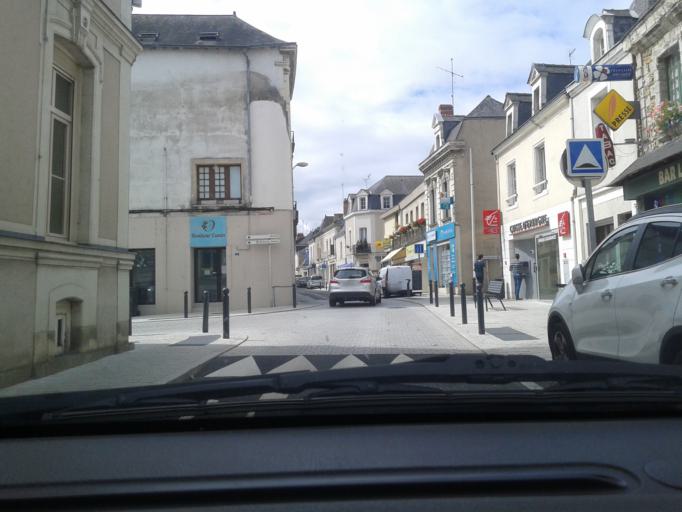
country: FR
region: Pays de la Loire
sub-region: Departement de Maine-et-Loire
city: Grez-Neuville
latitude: 47.6280
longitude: -0.7143
